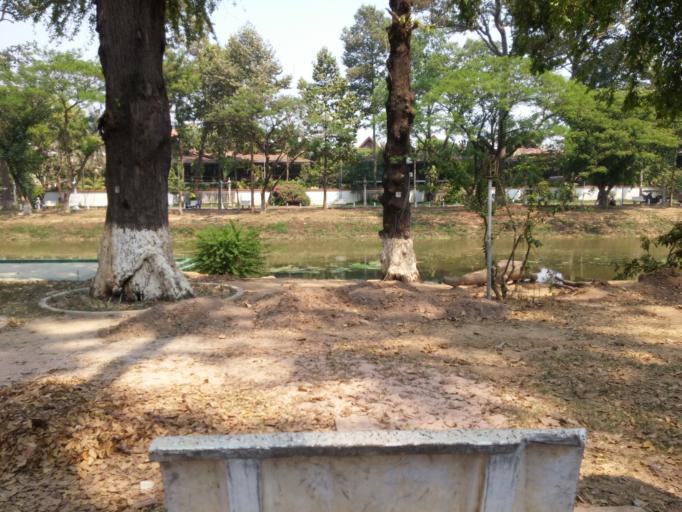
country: KH
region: Siem Reap
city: Siem Reap
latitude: 13.3586
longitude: 103.8587
